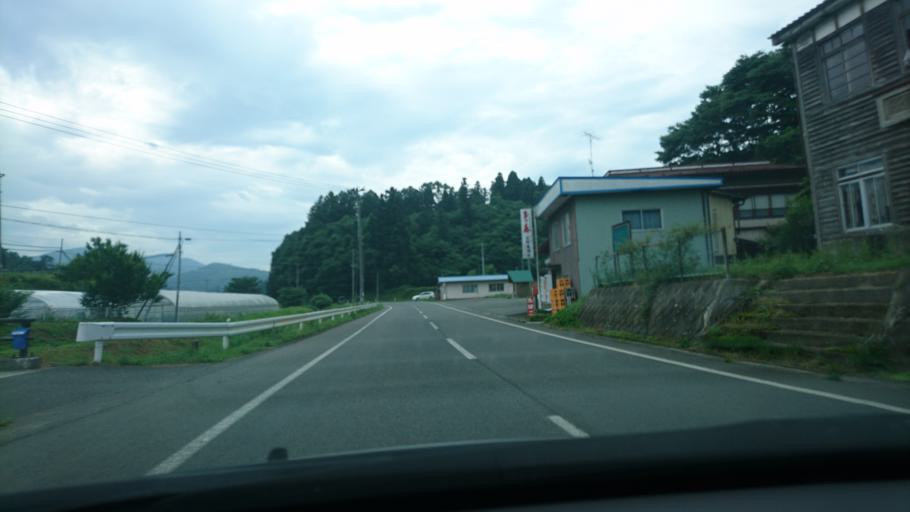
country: JP
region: Iwate
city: Ichinoseki
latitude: 38.9120
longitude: 141.4190
